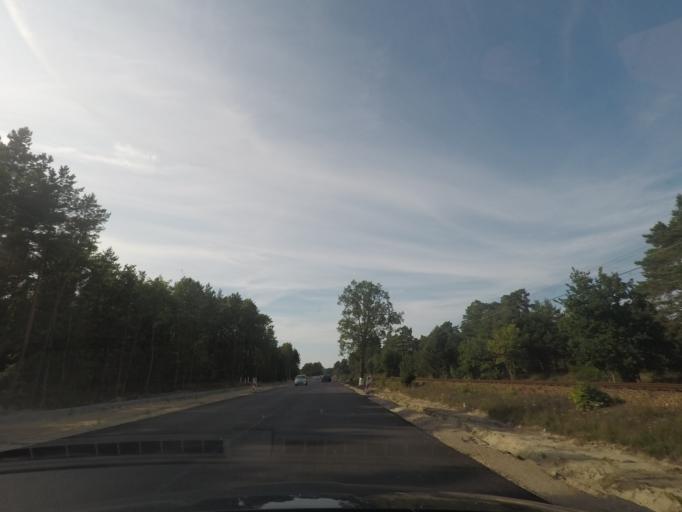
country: PL
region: Pomeranian Voivodeship
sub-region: Powiat leborski
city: Leba
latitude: 54.7220
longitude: 17.5721
